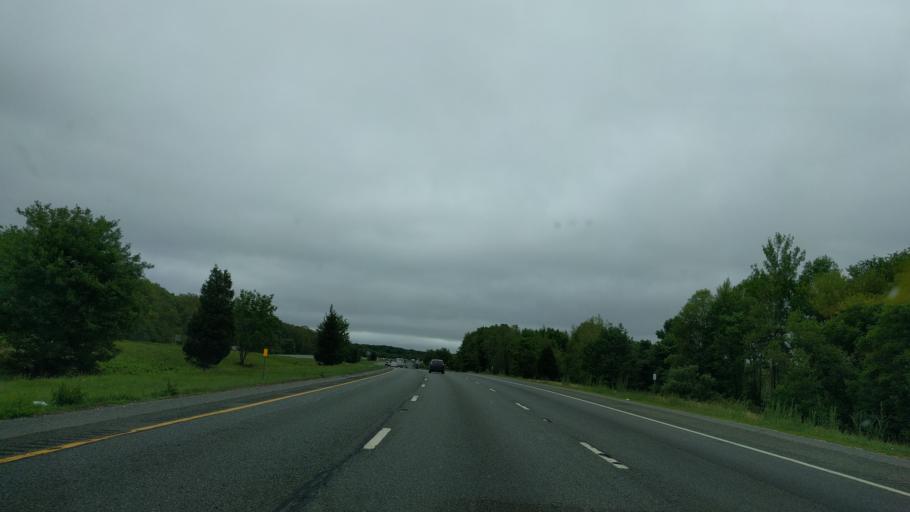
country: US
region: Rhode Island
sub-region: Providence County
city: Johnston
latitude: 41.8586
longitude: -71.5144
